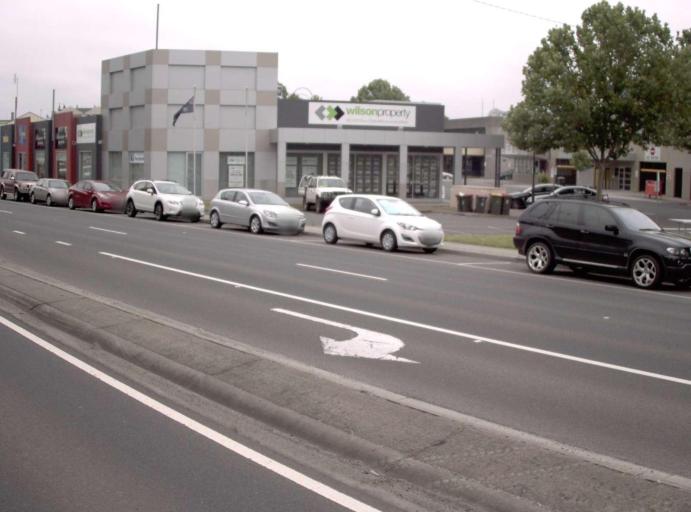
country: AU
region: Victoria
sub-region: Latrobe
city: Traralgon
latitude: -38.1979
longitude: 146.5395
